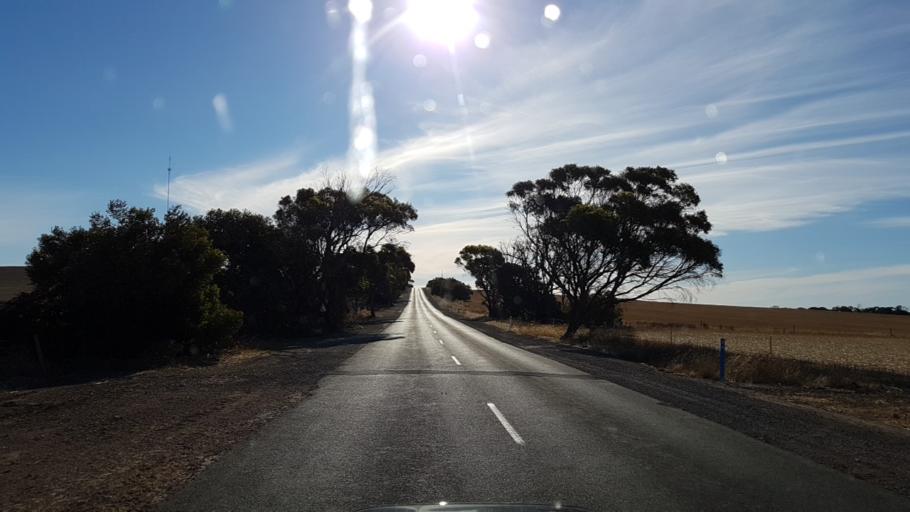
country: AU
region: South Australia
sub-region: Yorke Peninsula
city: Honiton
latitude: -34.9850
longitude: 137.2714
